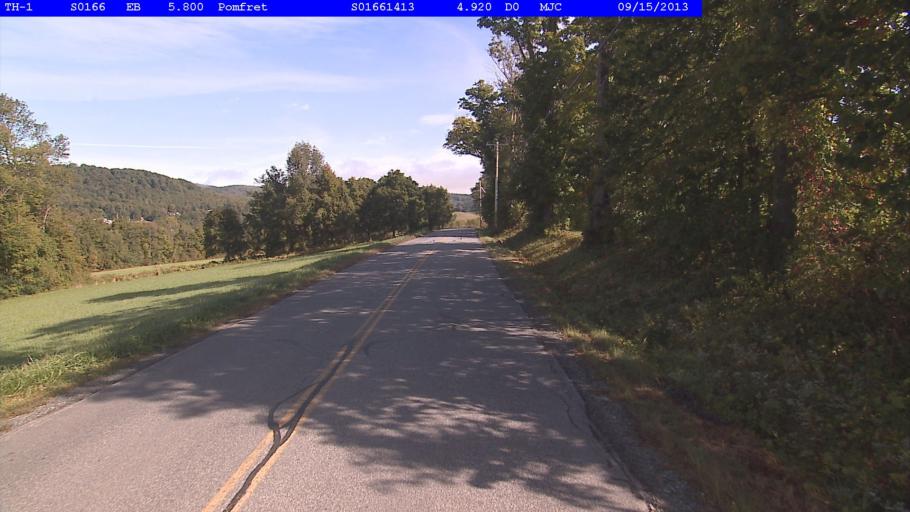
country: US
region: Vermont
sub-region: Windsor County
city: Woodstock
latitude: 43.7121
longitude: -72.5088
